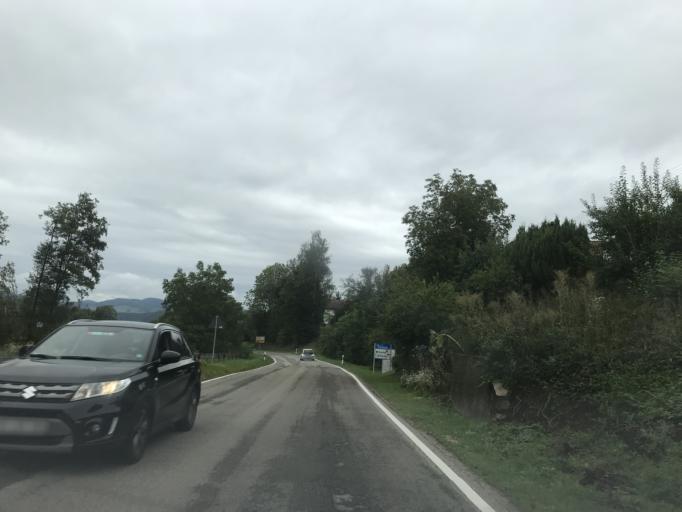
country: DE
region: Baden-Wuerttemberg
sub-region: Freiburg Region
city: Murg
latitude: 47.5819
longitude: 8.0327
